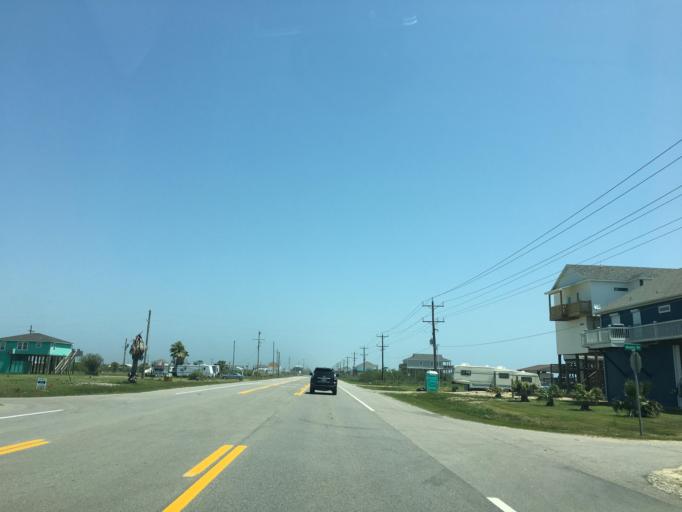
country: US
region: Texas
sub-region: Galveston County
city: Bolivar Peninsula
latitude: 29.5121
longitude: -94.4900
